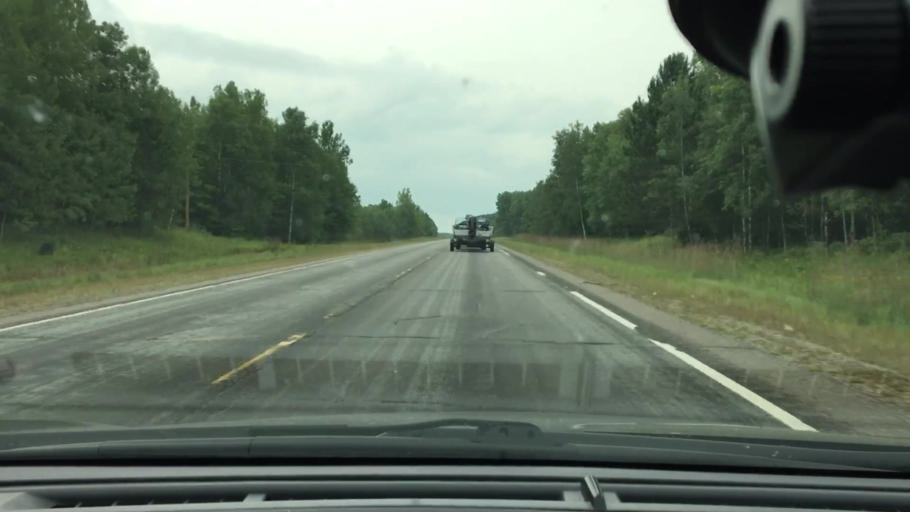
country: US
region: Minnesota
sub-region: Crow Wing County
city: Crosby
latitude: 46.6427
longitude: -93.9513
